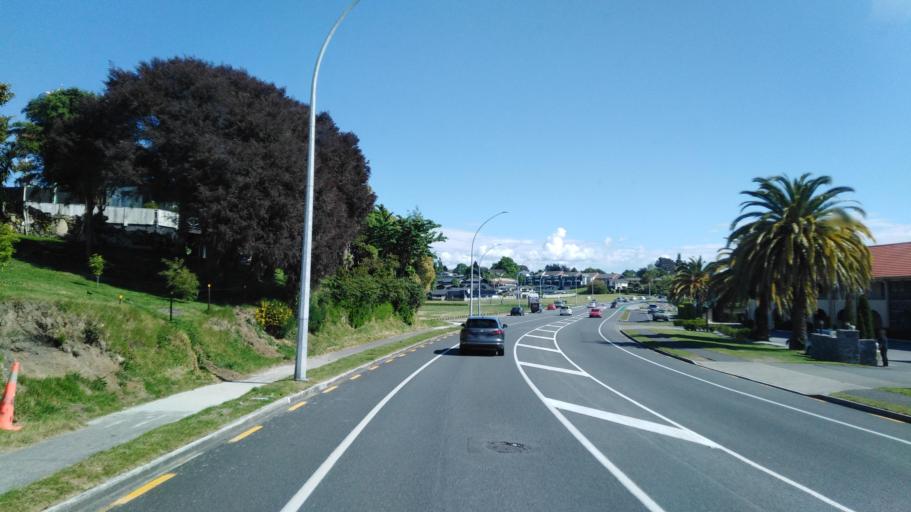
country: NZ
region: Waikato
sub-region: Taupo District
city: Taupo
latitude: -38.7082
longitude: 176.0887
